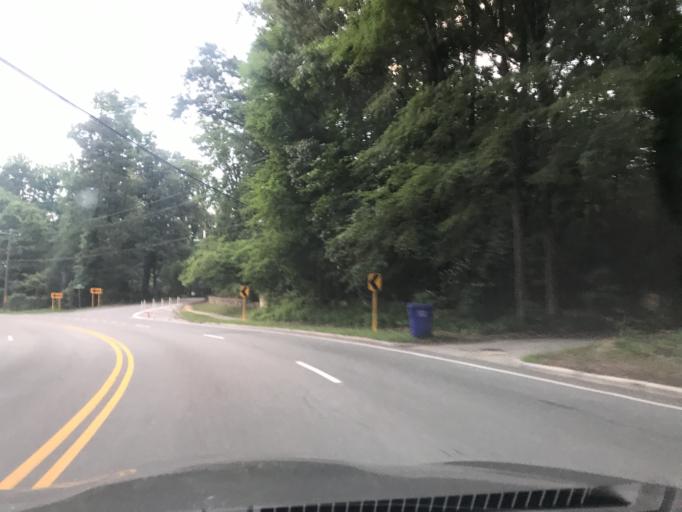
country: US
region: North Carolina
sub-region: Orange County
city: Chapel Hill
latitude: 35.9190
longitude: -79.0390
